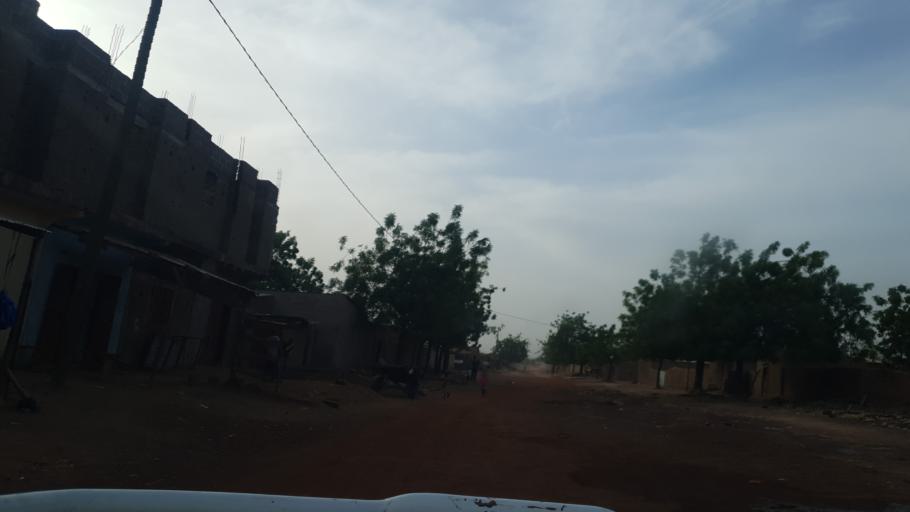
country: ML
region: Segou
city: Baroueli
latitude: 12.7799
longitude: -6.9439
